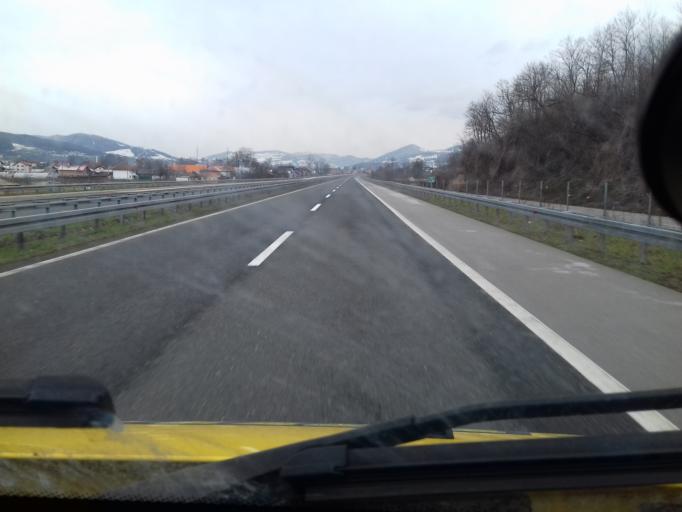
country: BA
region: Federation of Bosnia and Herzegovina
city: Dobrinje
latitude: 44.0331
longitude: 18.1247
